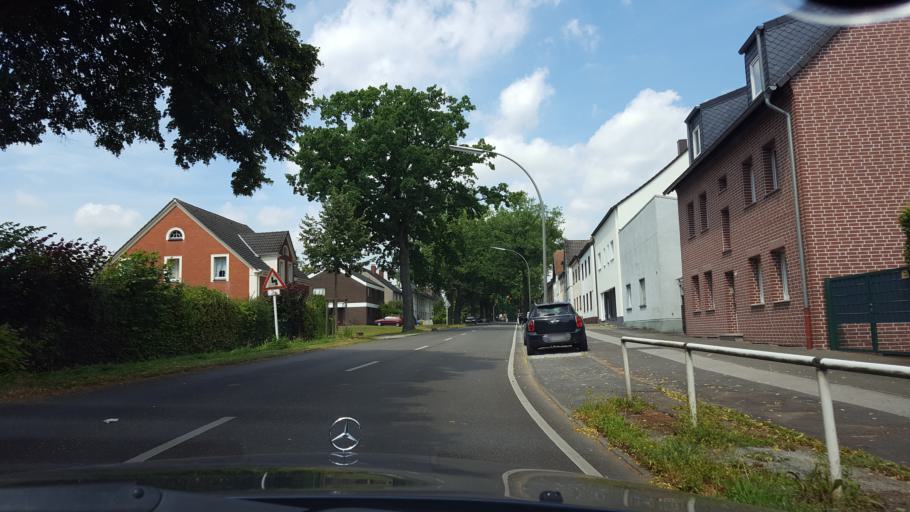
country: DE
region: North Rhine-Westphalia
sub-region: Regierungsbezirk Munster
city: Recklinghausen
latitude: 51.6627
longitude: 7.1809
